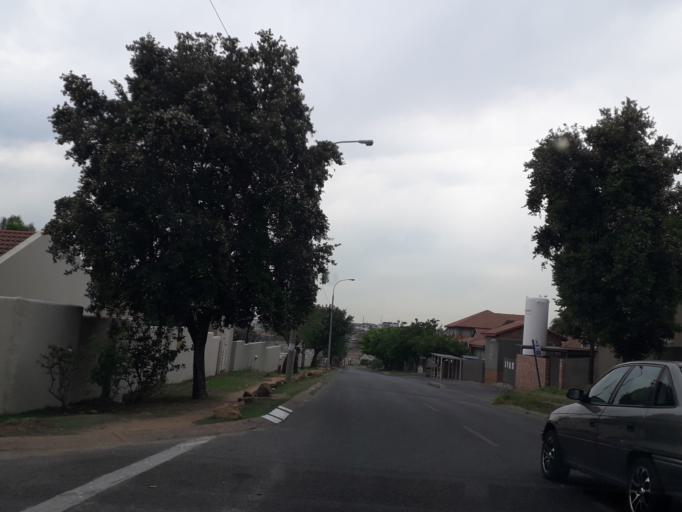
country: ZA
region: Gauteng
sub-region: City of Johannesburg Metropolitan Municipality
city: Roodepoort
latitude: -26.1005
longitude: 27.9242
